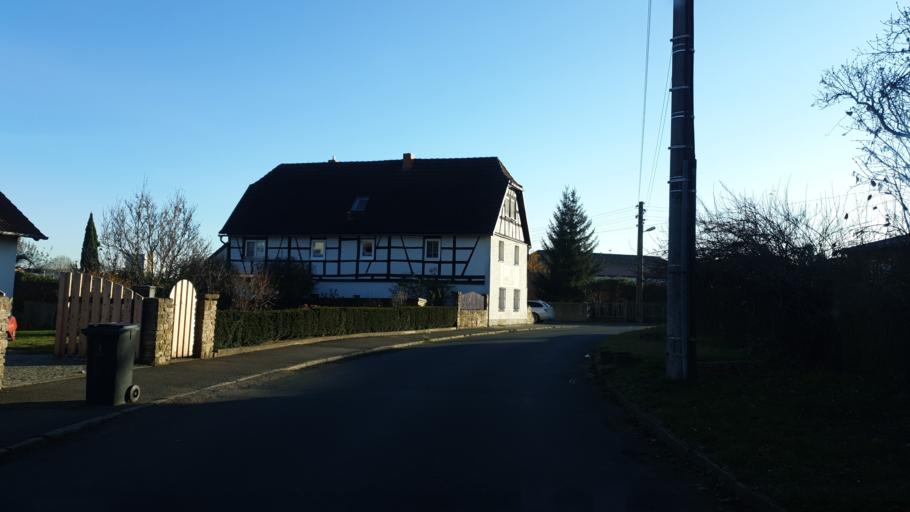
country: DE
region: Thuringia
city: Hartmannsdorf
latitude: 50.9747
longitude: 11.9752
